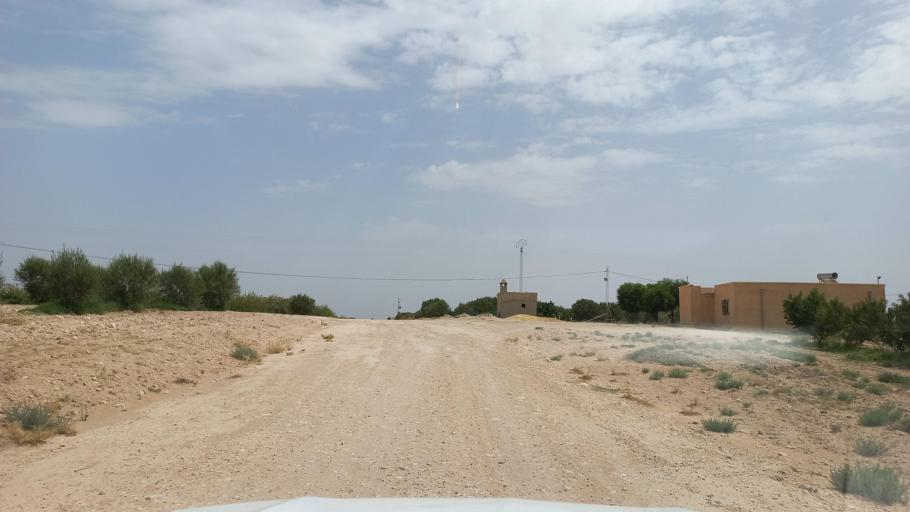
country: TN
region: Al Qasrayn
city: Kasserine
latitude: 35.2820
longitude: 9.0070
